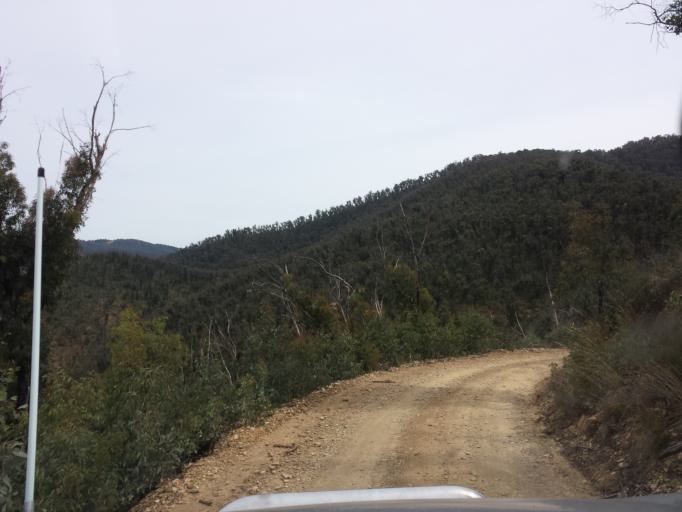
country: AU
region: Victoria
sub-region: Wellington
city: Heyfield
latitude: -37.7404
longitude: 146.4010
